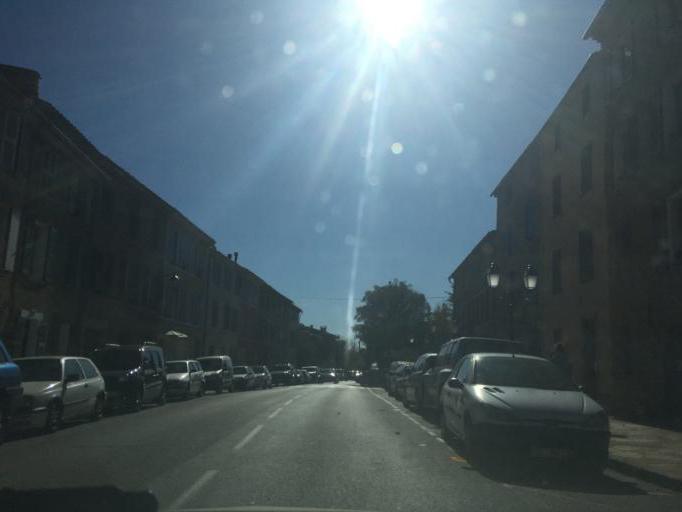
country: FR
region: Provence-Alpes-Cote d'Azur
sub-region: Departement du Var
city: La Garde-Freinet
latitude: 43.3163
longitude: 6.4706
